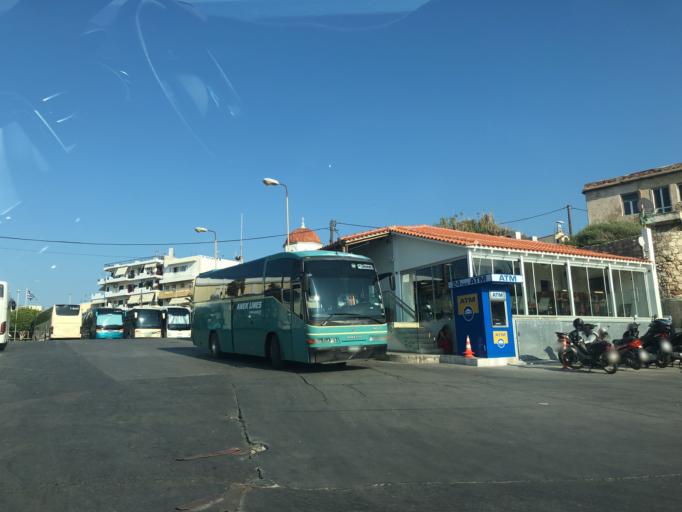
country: GR
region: Crete
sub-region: Nomos Rethymnis
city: Rethymno
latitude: 35.3665
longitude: 24.4681
